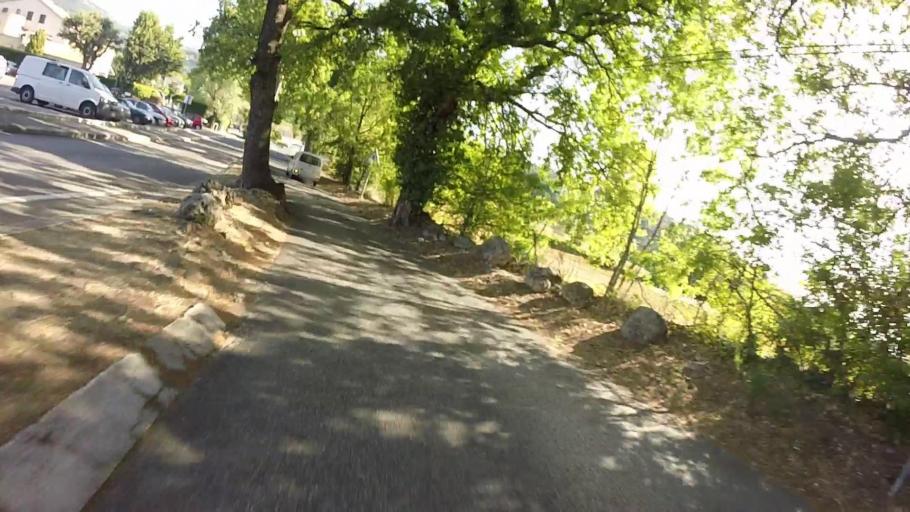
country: FR
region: Provence-Alpes-Cote d'Azur
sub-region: Departement des Alpes-Maritimes
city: Chateauneuf-Grasse
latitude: 43.6607
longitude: 6.9876
